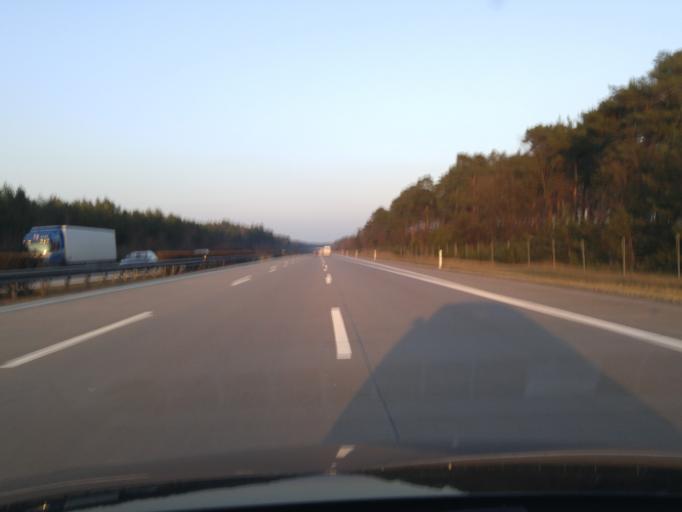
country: DE
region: Brandenburg
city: Wollin
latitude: 52.3225
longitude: 12.4945
